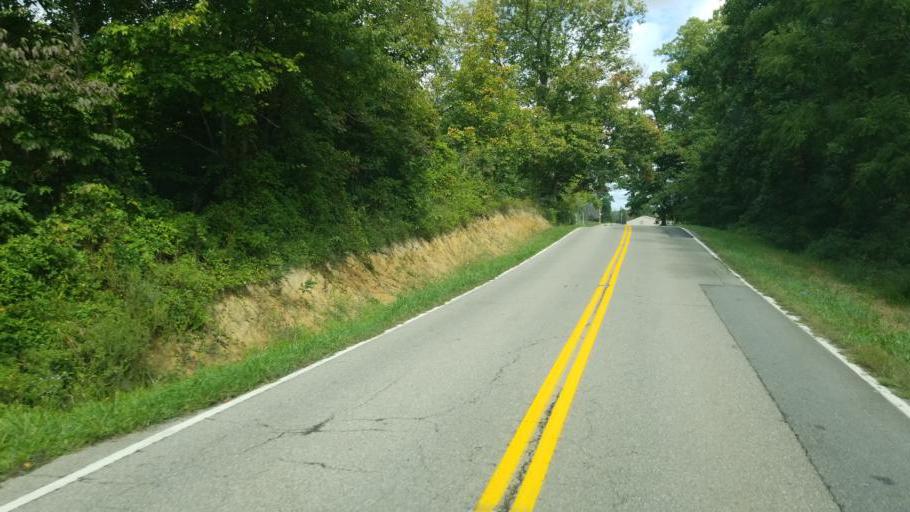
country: US
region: Ohio
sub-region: Jackson County
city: Oak Hill
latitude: 38.8948
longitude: -82.6548
